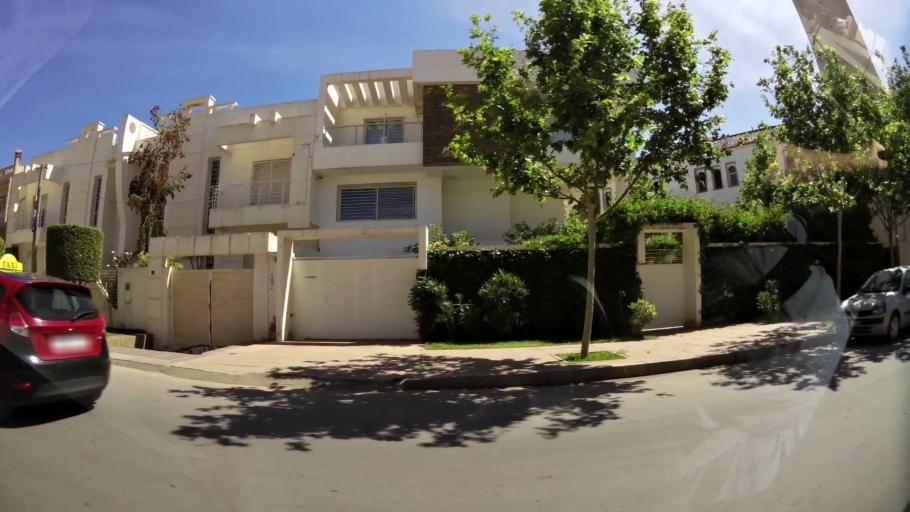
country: MA
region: Oriental
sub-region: Oujda-Angad
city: Oujda
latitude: 34.6570
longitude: -1.9068
